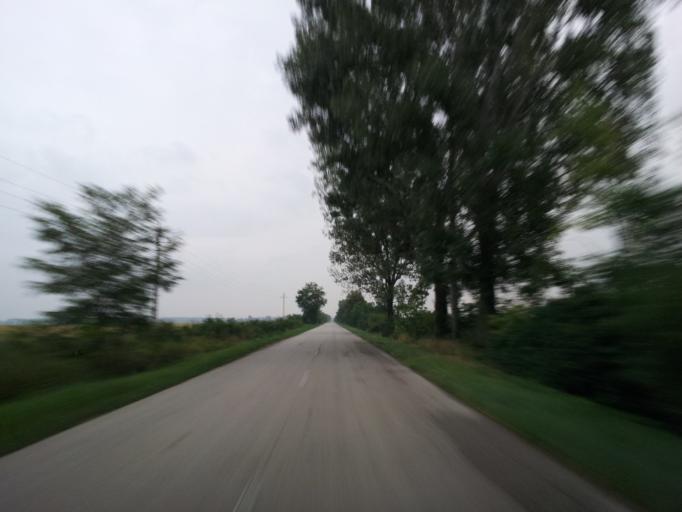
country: HU
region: Tolna
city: Fadd
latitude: 46.4867
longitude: 18.8527
